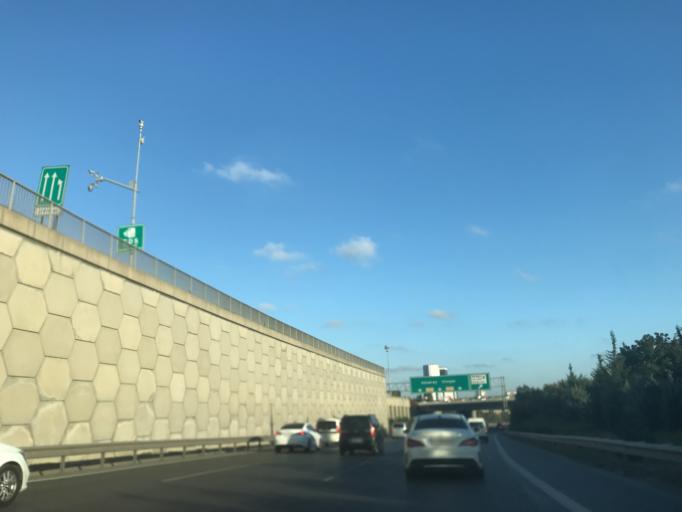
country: TR
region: Istanbul
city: Mahmutbey
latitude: 41.0619
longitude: 28.8403
